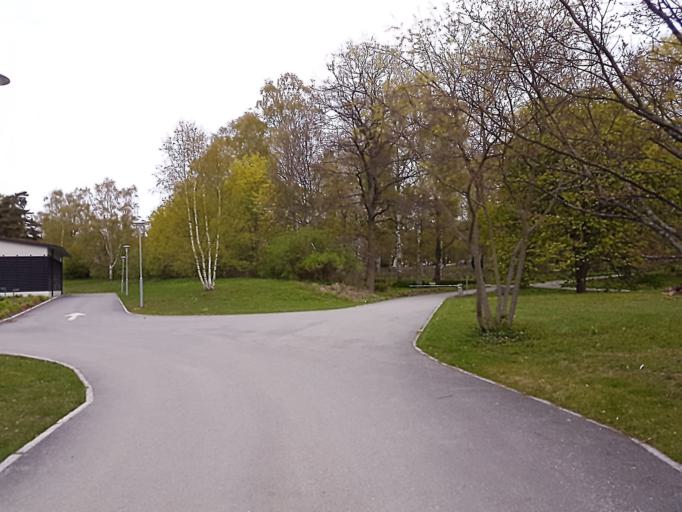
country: SE
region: Stockholm
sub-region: Solna Kommun
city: Solna
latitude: 59.3601
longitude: 18.0181
